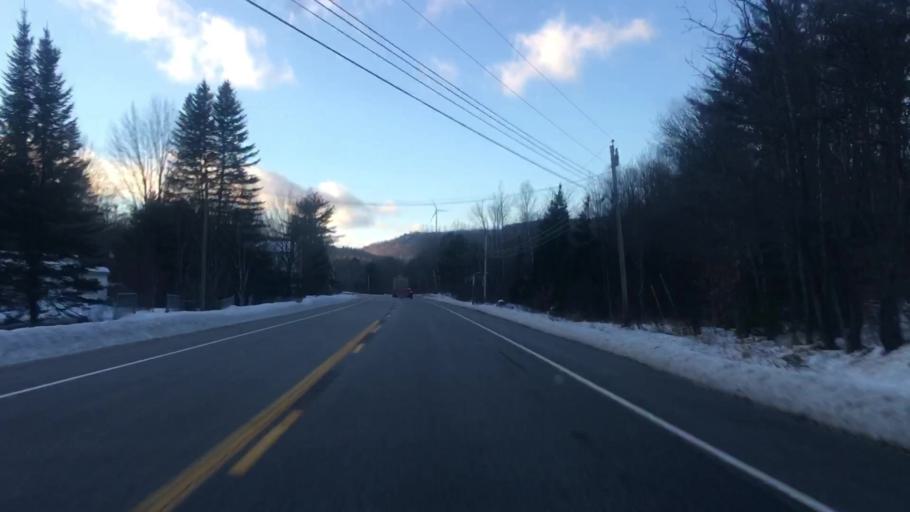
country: US
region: Maine
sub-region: Oxford County
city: Peru
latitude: 44.5858
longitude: -70.3433
